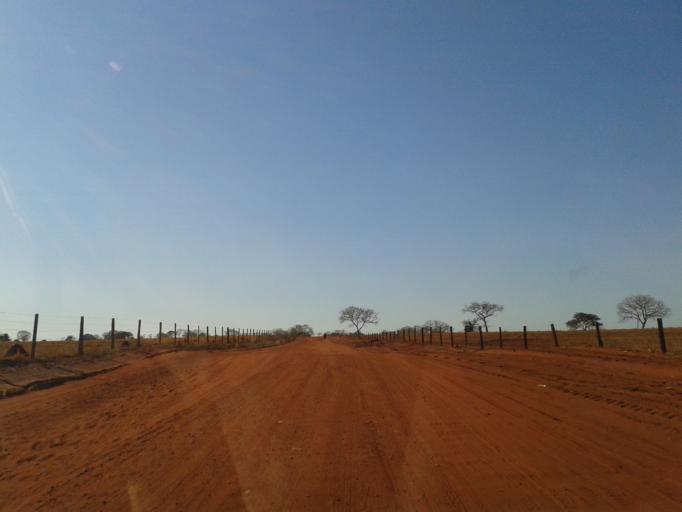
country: BR
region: Minas Gerais
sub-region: Ituiutaba
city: Ituiutaba
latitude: -18.9793
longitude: -49.4077
